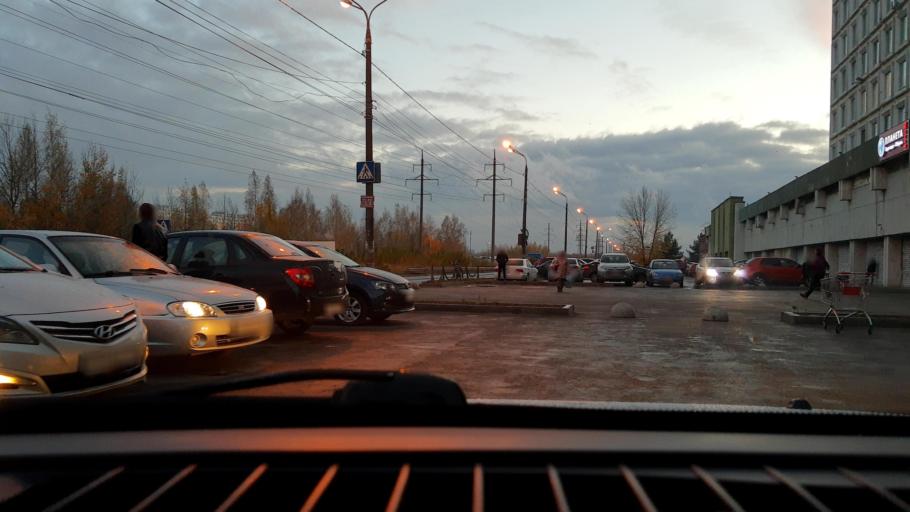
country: RU
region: Nizjnij Novgorod
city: Gorbatovka
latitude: 56.3669
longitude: 43.7955
